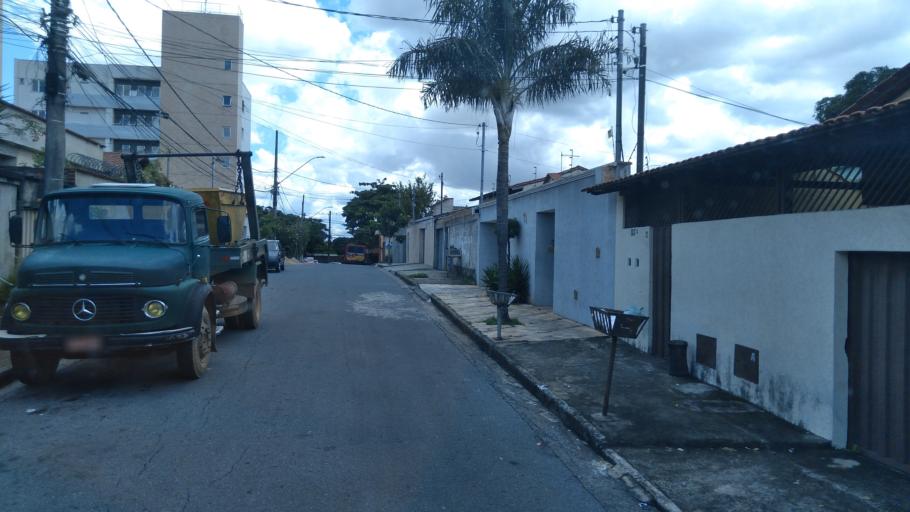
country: BR
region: Minas Gerais
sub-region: Belo Horizonte
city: Belo Horizonte
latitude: -19.8912
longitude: -43.9058
